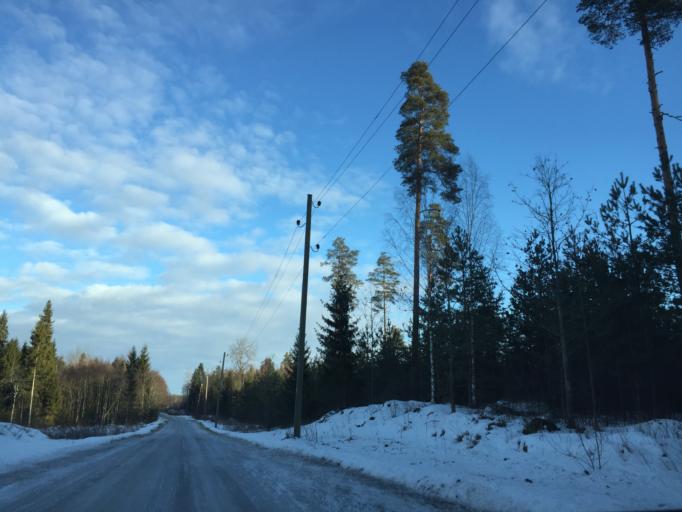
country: LV
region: Kegums
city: Kegums
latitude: 56.7364
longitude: 24.6644
